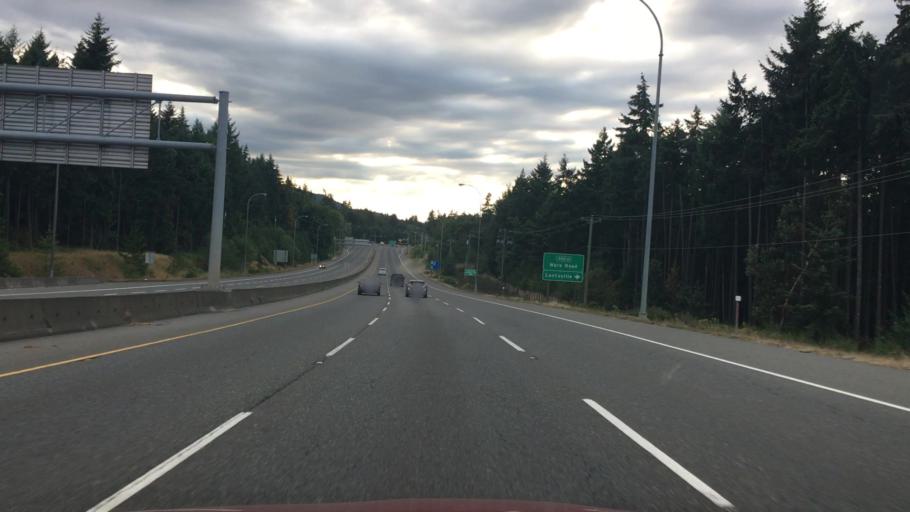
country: CA
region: British Columbia
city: Nanaimo
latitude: 49.2435
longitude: -124.0681
